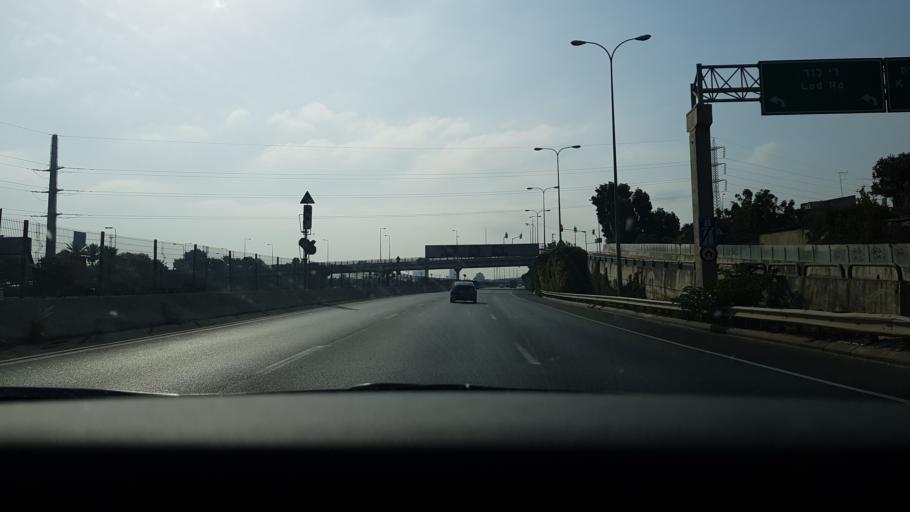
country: IL
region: Tel Aviv
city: Azor
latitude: 32.0486
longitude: 34.7854
